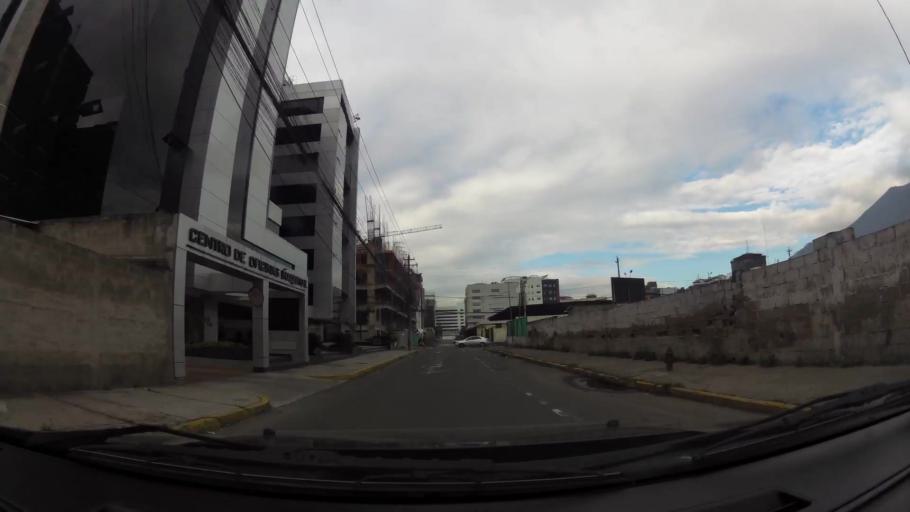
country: EC
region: Pichincha
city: Quito
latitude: -0.1711
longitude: -78.4855
